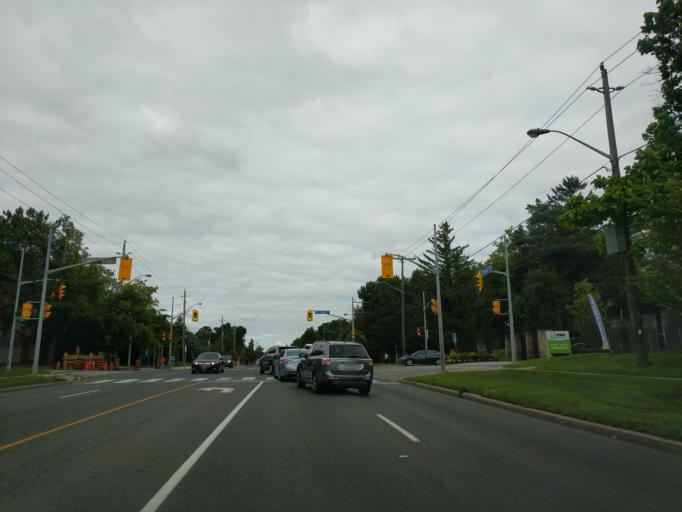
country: CA
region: Ontario
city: Willowdale
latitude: 43.8039
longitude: -79.3932
